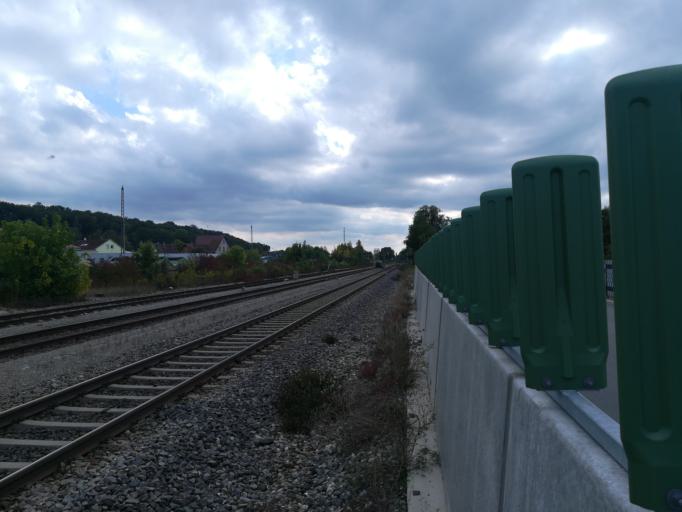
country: DE
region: Baden-Wuerttemberg
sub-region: Tuebingen Region
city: Riedlingen
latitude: 48.1515
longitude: 9.4865
